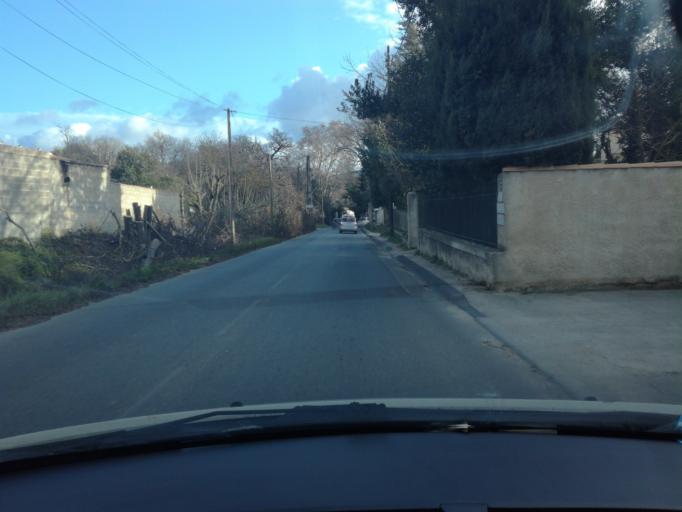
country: FR
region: Provence-Alpes-Cote d'Azur
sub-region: Departement des Bouches-du-Rhone
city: La Penne-sur-Huveaune
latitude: 43.3029
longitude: 5.5009
